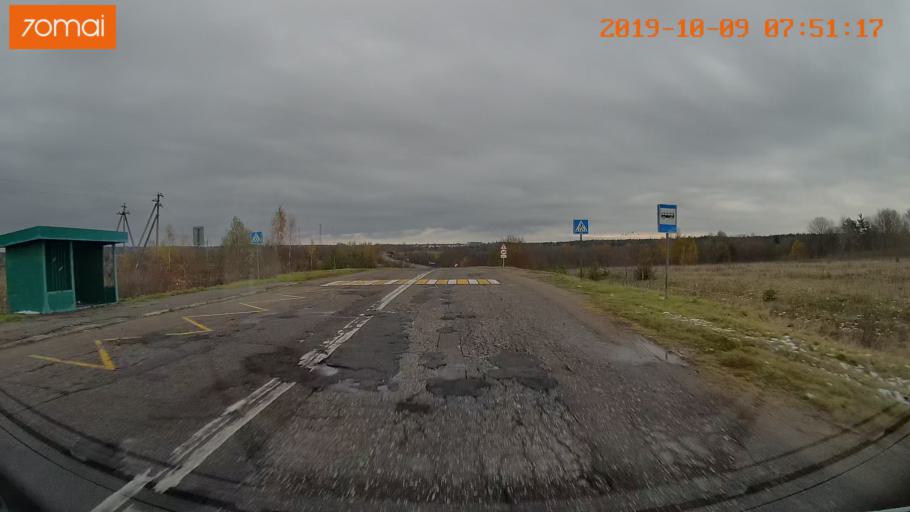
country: RU
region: Jaroslavl
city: Kukoboy
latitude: 58.6797
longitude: 39.8728
